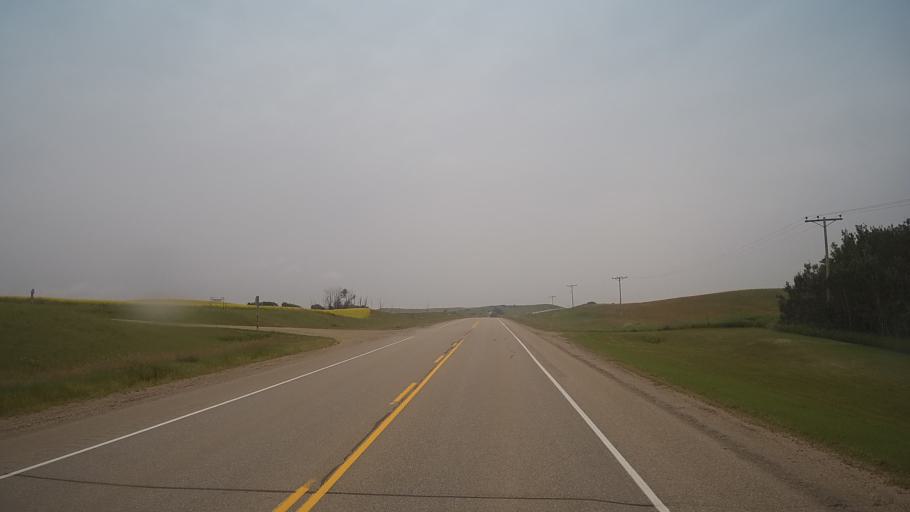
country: CA
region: Saskatchewan
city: Biggar
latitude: 52.0564
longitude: -107.8589
